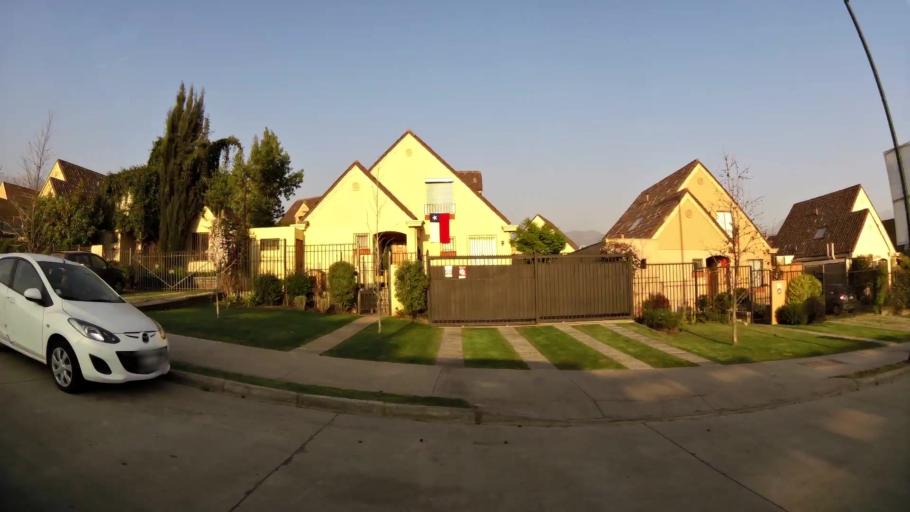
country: CL
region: Santiago Metropolitan
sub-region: Provincia de Chacabuco
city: Chicureo Abajo
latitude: -33.3241
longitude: -70.5157
